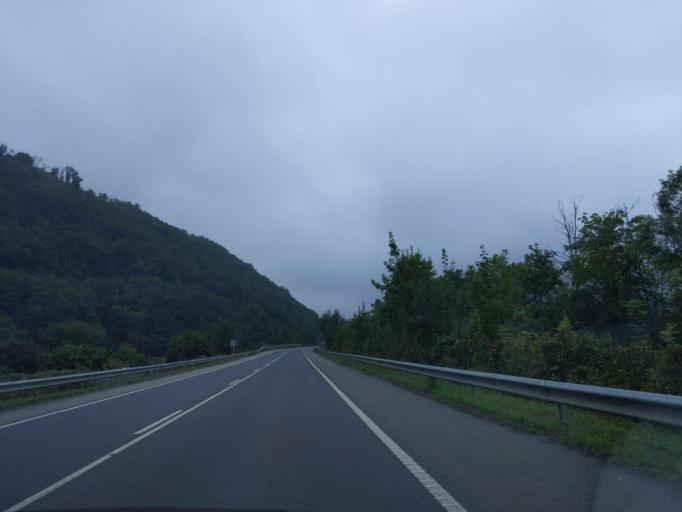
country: ES
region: Asturias
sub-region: Province of Asturias
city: Pola de Laviana
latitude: 43.2541
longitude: -5.5728
